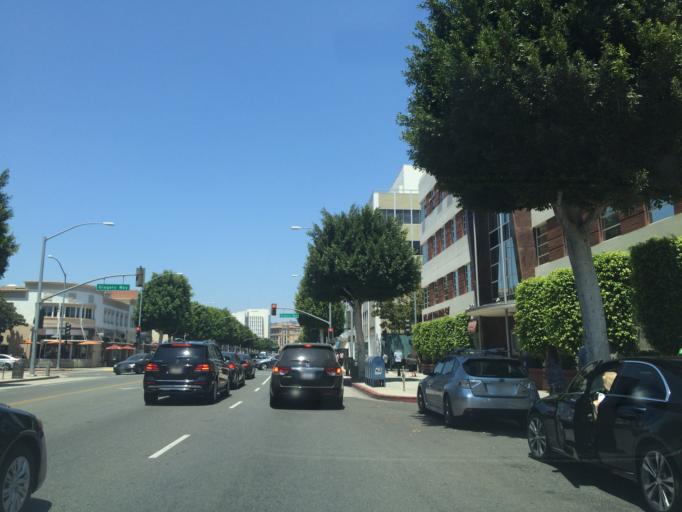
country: US
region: California
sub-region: Los Angeles County
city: Beverly Hills
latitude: 34.0617
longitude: -118.3990
